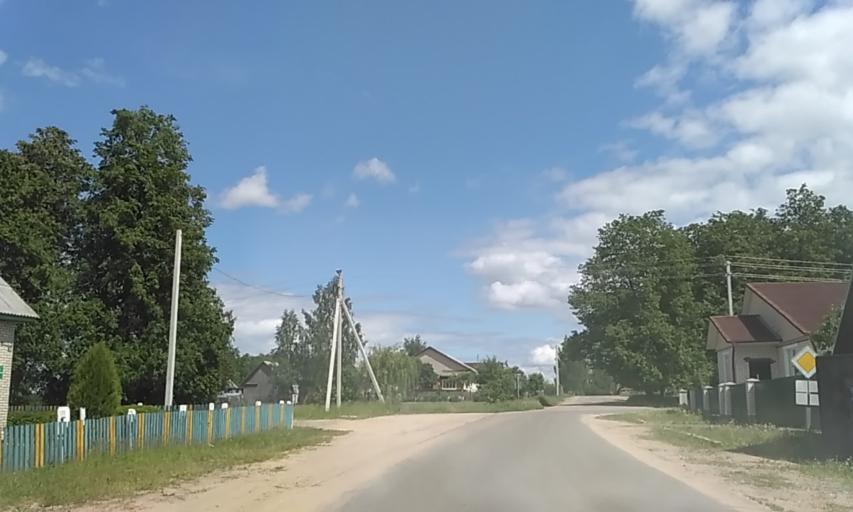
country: BY
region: Minsk
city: Krupki
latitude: 54.3628
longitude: 29.1066
